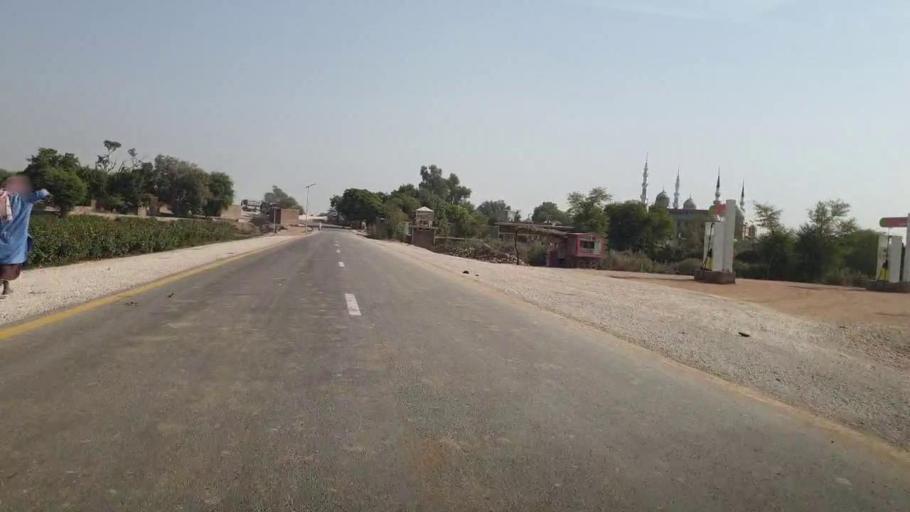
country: PK
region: Sindh
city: Bhan
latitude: 26.5634
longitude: 67.7725
